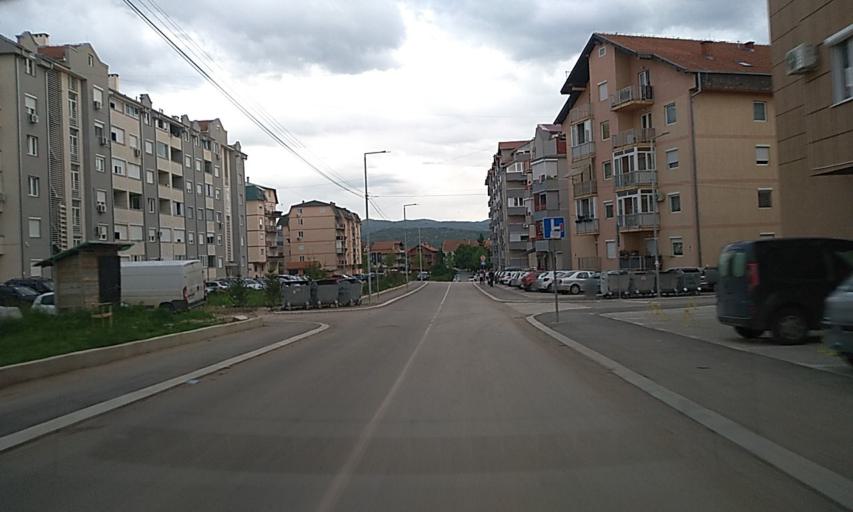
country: RS
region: Central Serbia
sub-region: Nisavski Okrug
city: Nis
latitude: 43.3377
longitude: 21.9229
